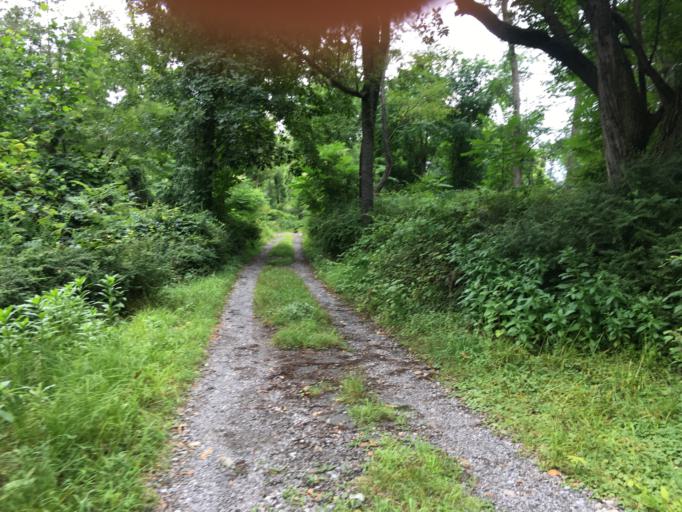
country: US
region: New York
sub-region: Orange County
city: Fort Montgomery
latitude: 41.2997
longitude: -73.9917
